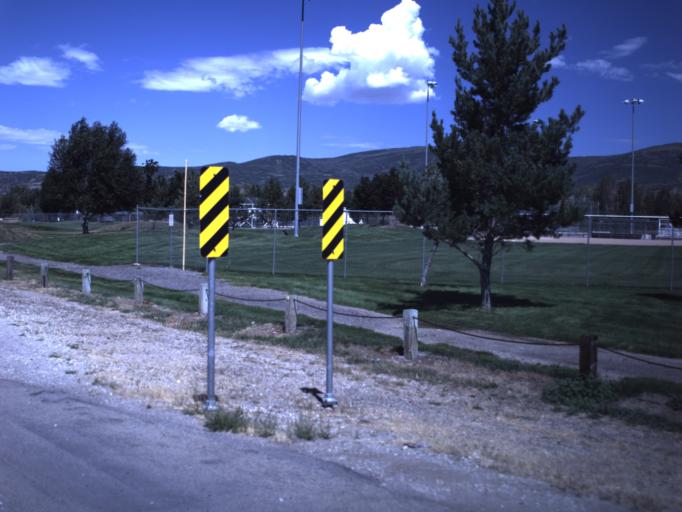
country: US
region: Utah
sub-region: Summit County
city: Oakley
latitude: 40.7070
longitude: -111.2883
